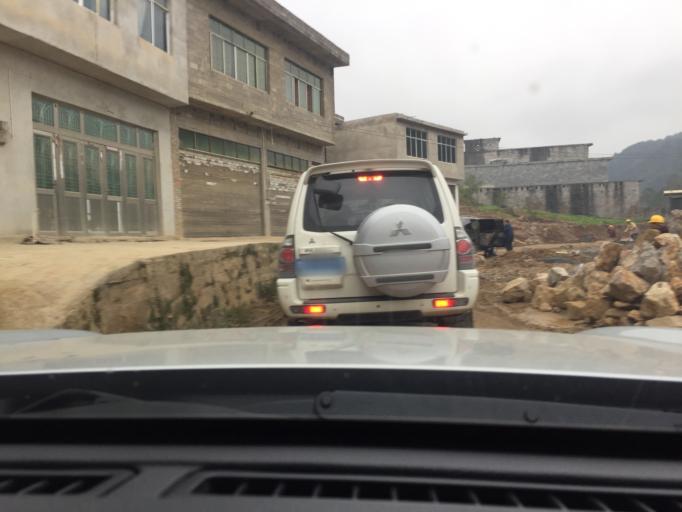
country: CN
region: Guizhou Sheng
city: Fuxing
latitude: 28.0864
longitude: 107.9041
